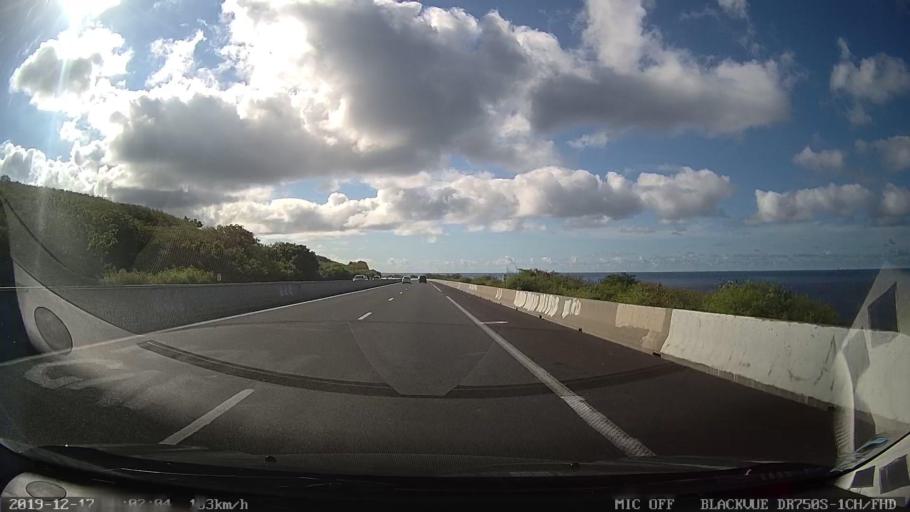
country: RE
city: Piton Saint-Leu
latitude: -21.2382
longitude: 55.3147
